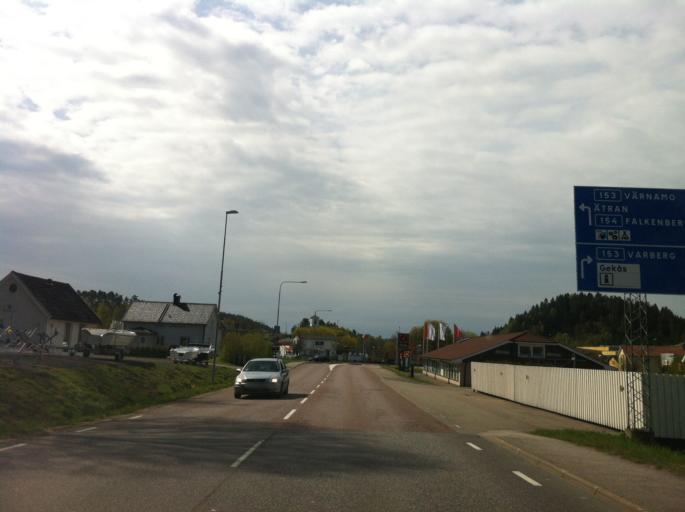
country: SE
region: Halland
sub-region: Halmstads Kommun
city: Getinge
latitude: 57.1377
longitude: 12.7194
